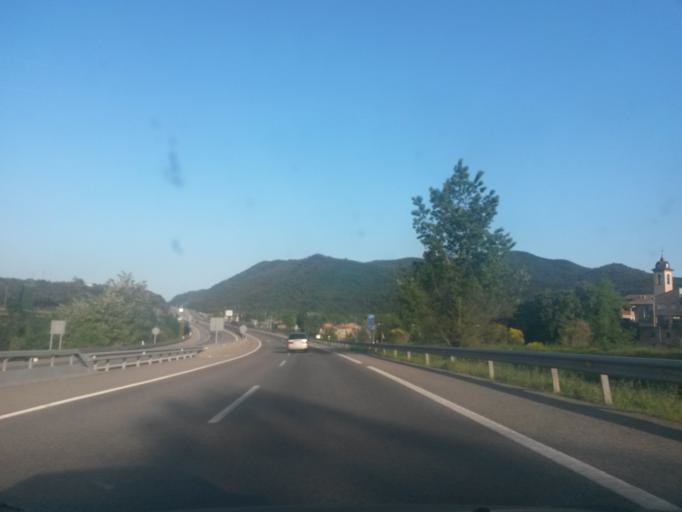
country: ES
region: Catalonia
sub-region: Provincia de Girona
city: Argelaguer
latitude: 42.2143
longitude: 2.6074
